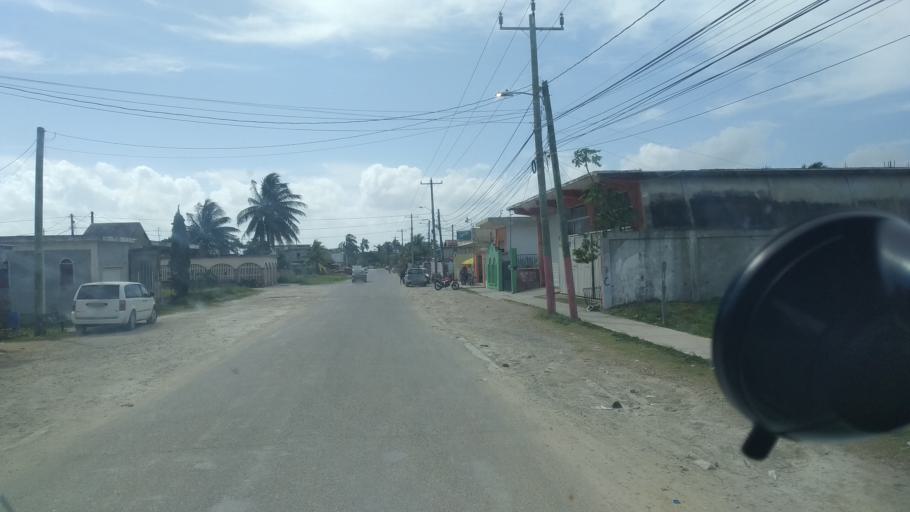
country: BZ
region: Corozal
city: Corozal
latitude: 18.4004
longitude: -88.3822
